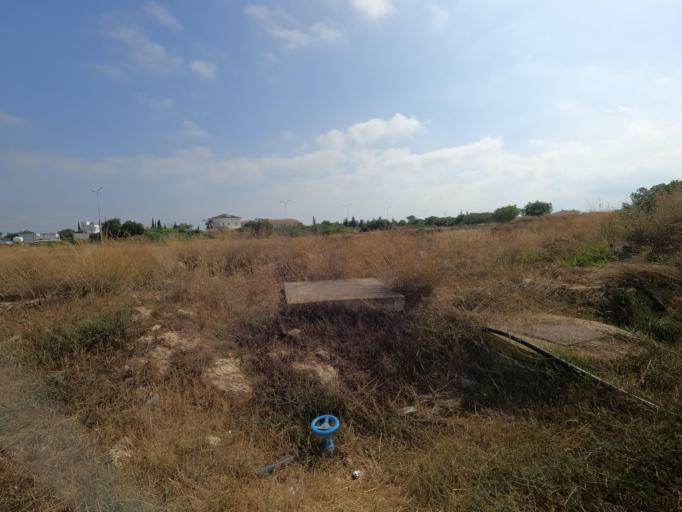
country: CY
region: Ammochostos
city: Paralimni
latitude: 35.0291
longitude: 34.0041
